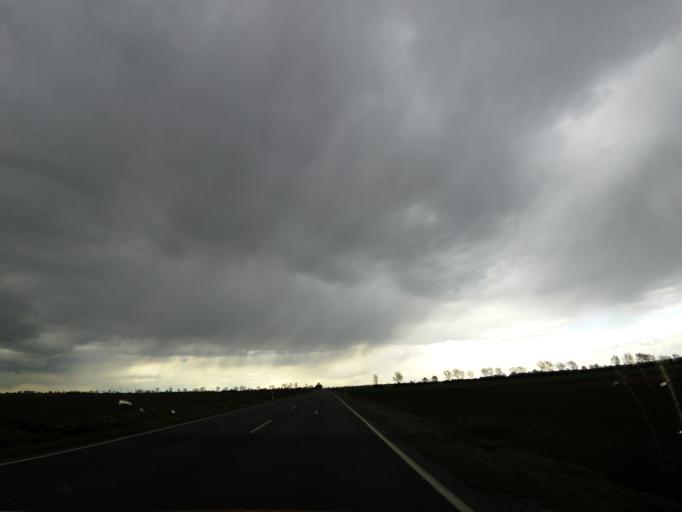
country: DE
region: Saxony-Anhalt
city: Kroppenstedt
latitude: 51.9404
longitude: 11.3457
